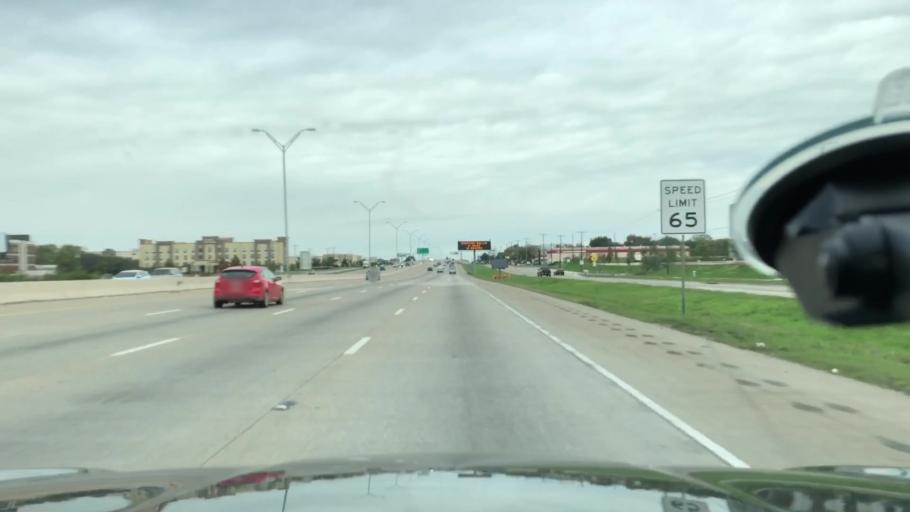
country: US
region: Texas
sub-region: Dallas County
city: DeSoto
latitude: 32.6230
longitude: -96.8229
